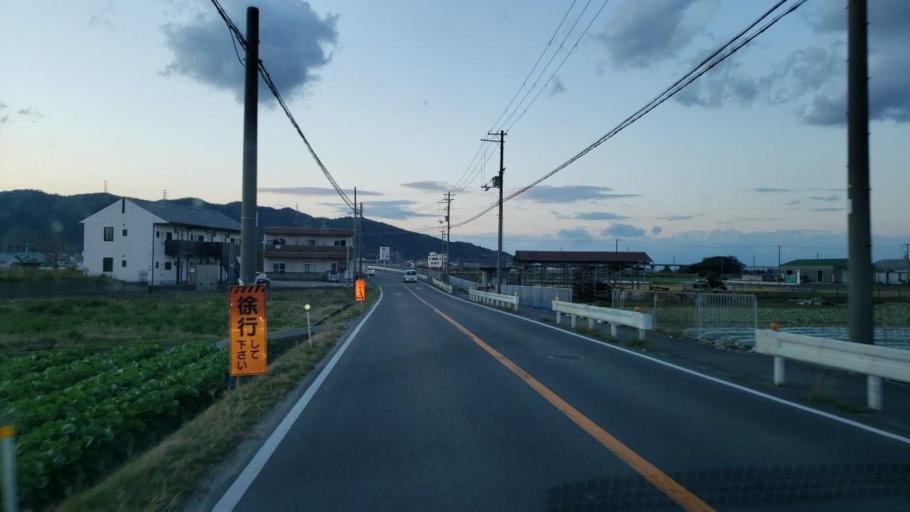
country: JP
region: Hyogo
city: Fukura
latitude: 34.3013
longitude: 134.7521
